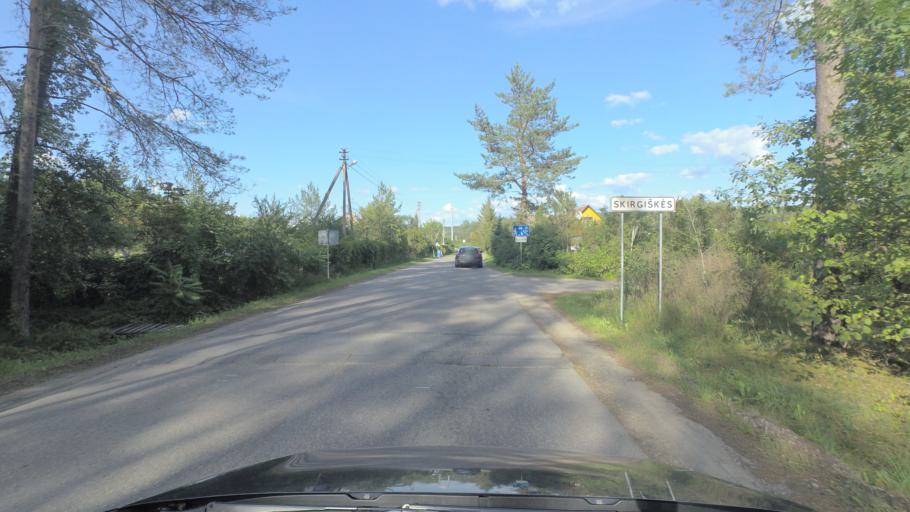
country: LT
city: Nemencine
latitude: 54.8268
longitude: 25.3610
